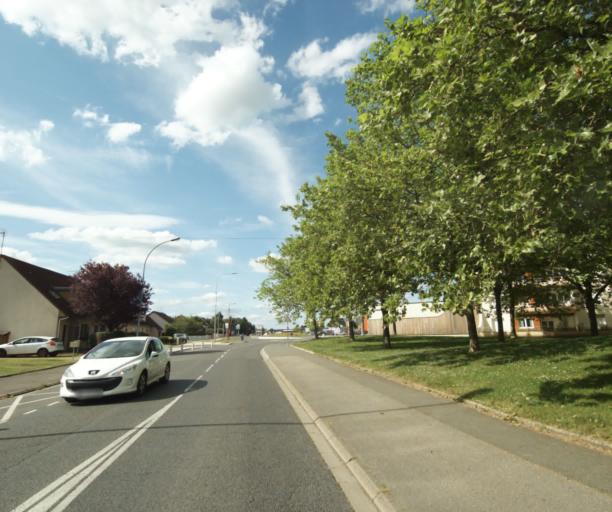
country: FR
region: Centre
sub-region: Departement d'Eure-et-Loir
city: Luce
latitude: 48.4331
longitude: 1.4438
